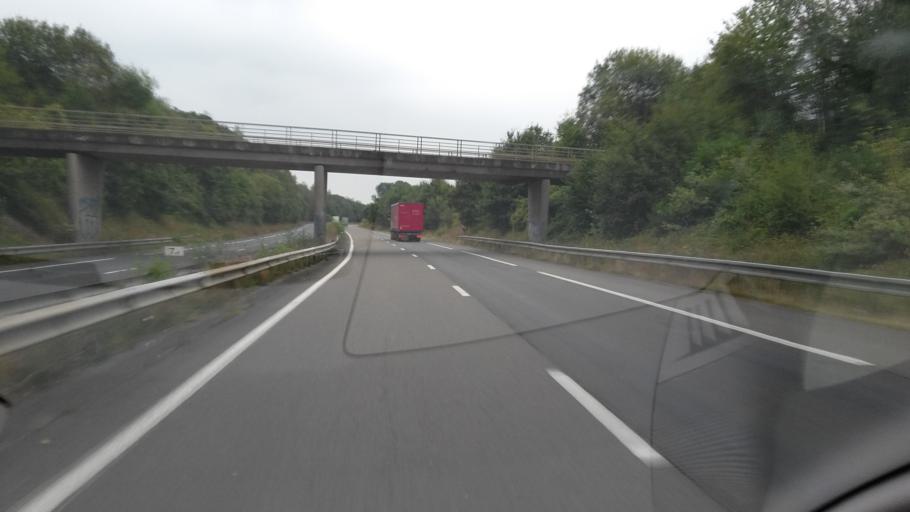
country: FR
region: Champagne-Ardenne
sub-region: Departement des Ardennes
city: Bazeilles
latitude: 49.7075
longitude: 5.0108
